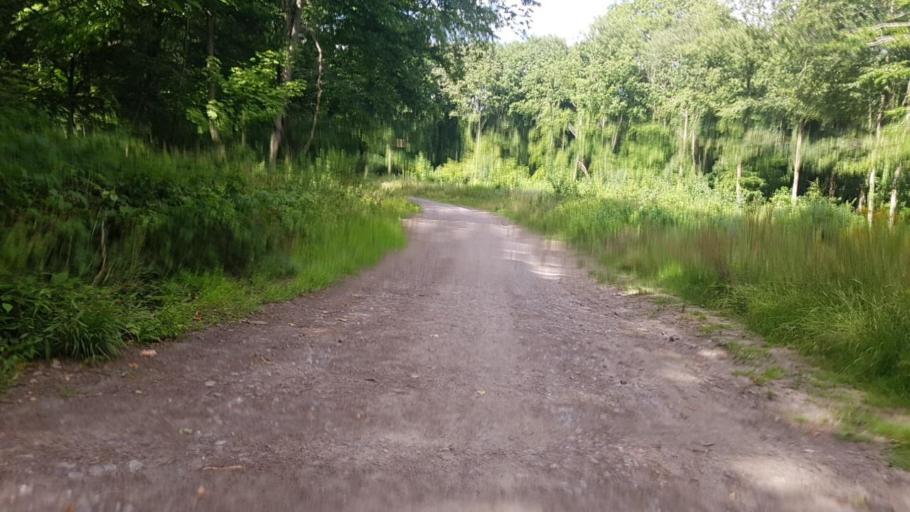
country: BE
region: Wallonia
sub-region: Province du Hainaut
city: Charleroi
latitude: 50.3636
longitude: 4.4525
